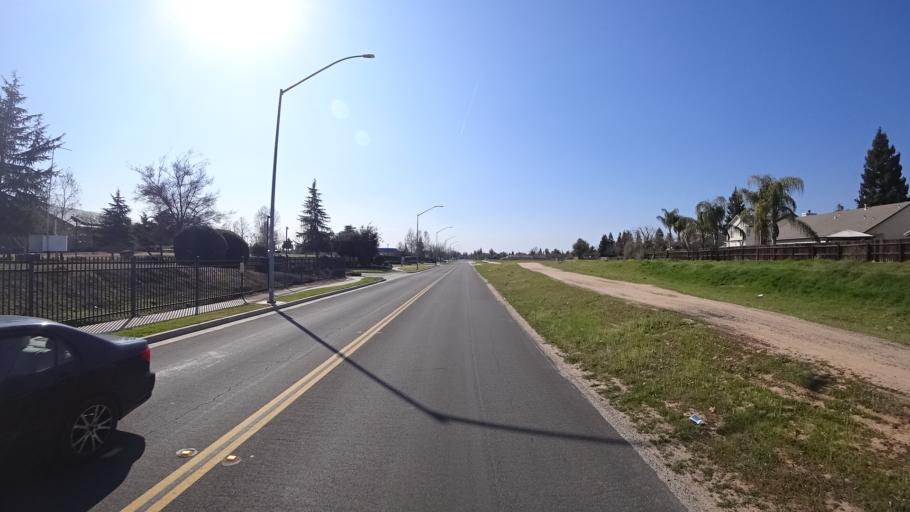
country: US
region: California
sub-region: Fresno County
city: Clovis
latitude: 36.8848
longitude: -119.7387
